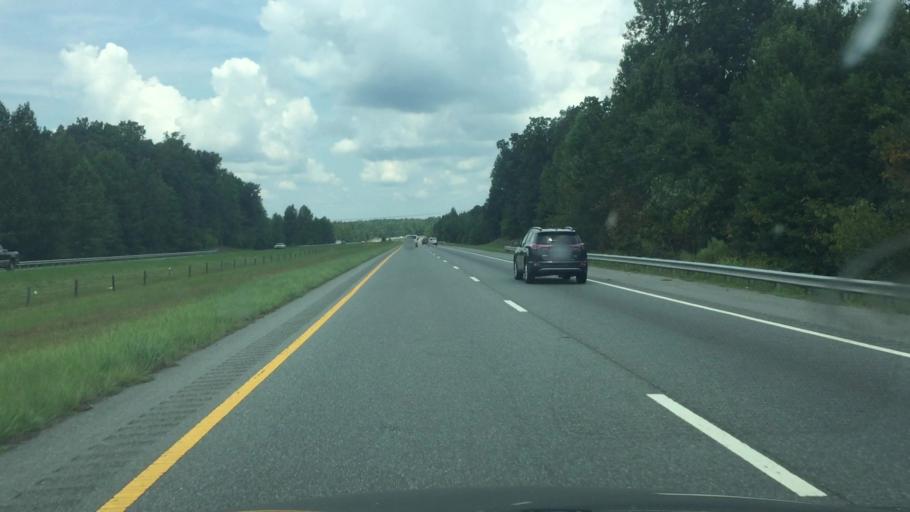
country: US
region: North Carolina
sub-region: Randolph County
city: Asheboro
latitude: 35.5544
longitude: -79.8000
